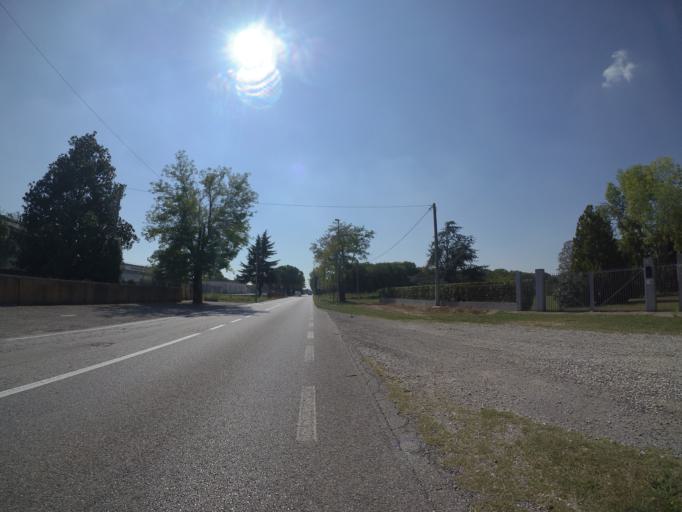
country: IT
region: Friuli Venezia Giulia
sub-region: Provincia di Udine
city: Codroipo
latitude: 45.9766
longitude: 12.9899
